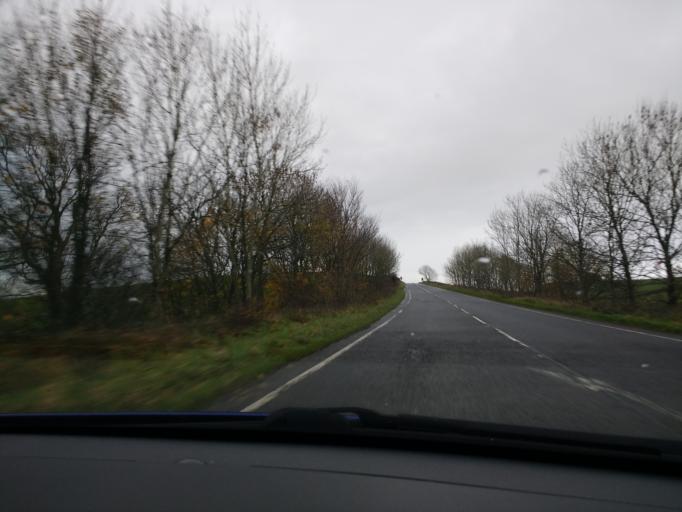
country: GB
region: England
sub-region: Cumbria
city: Millom
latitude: 54.2642
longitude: -3.2624
